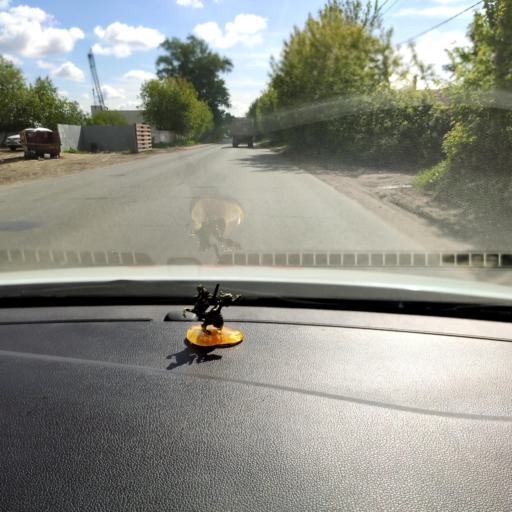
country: RU
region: Tatarstan
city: Staroye Arakchino
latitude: 55.8041
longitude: 49.0154
